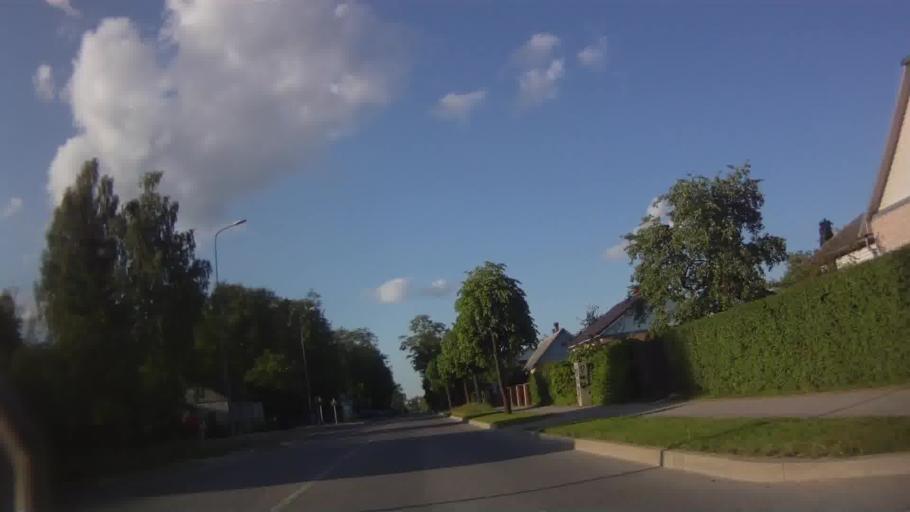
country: LV
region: Rezekne
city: Rezekne
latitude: 56.5110
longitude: 27.3396
